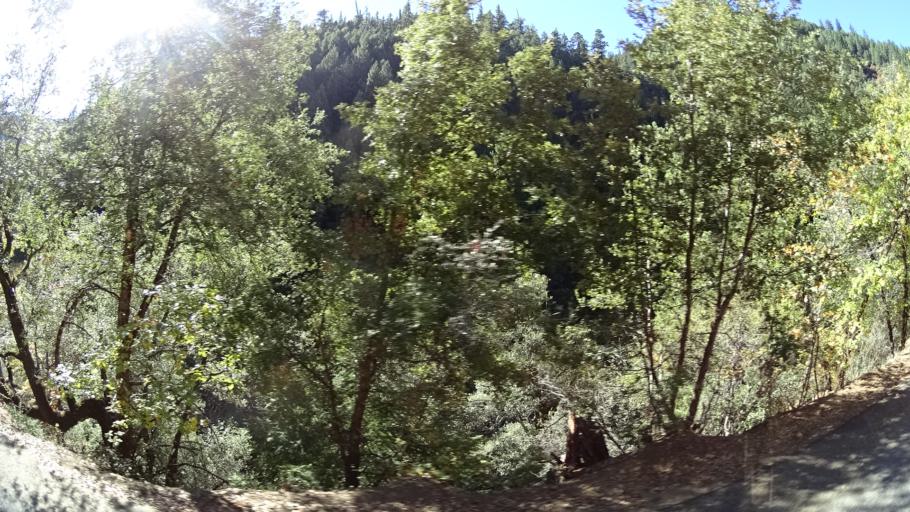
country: US
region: California
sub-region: Humboldt County
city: Willow Creek
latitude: 41.1650
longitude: -123.2134
